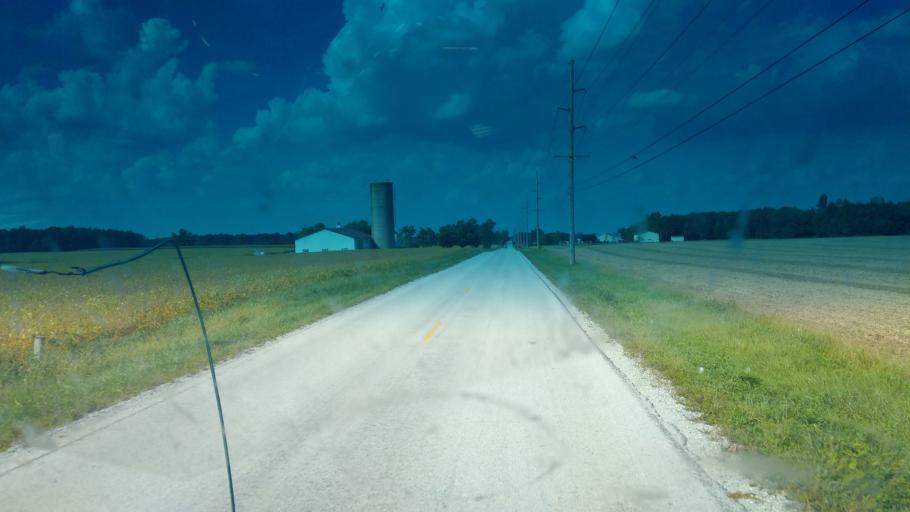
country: US
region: Ohio
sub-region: Hardin County
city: Kenton
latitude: 40.7483
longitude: -83.6524
